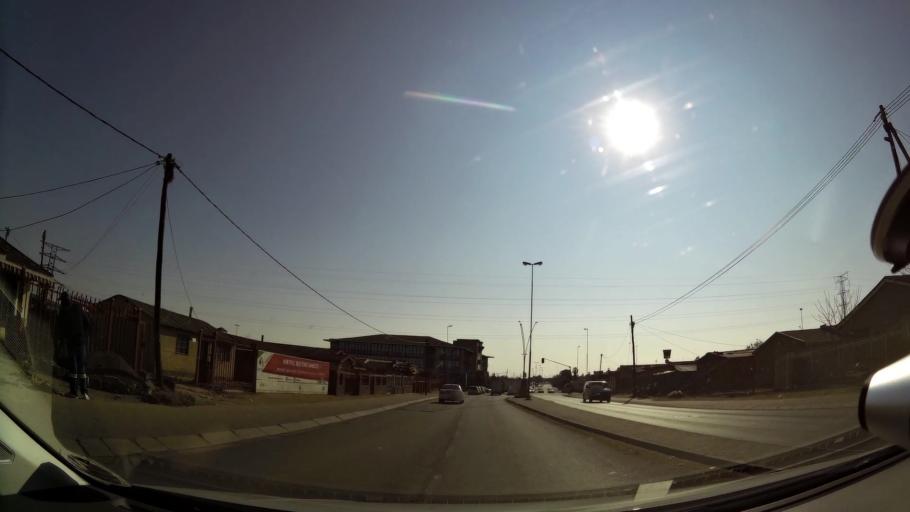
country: ZA
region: Orange Free State
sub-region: Mangaung Metropolitan Municipality
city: Bloemfontein
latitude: -29.1707
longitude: 26.2354
